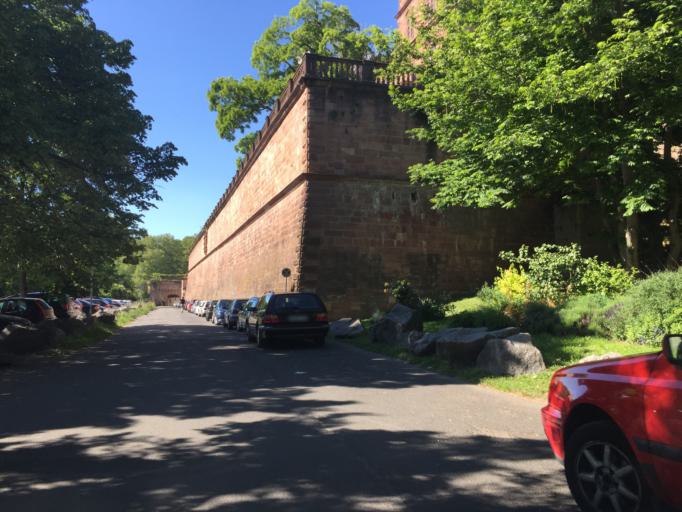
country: DE
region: Bavaria
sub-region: Regierungsbezirk Unterfranken
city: Aschaffenburg
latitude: 49.9750
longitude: 9.1416
